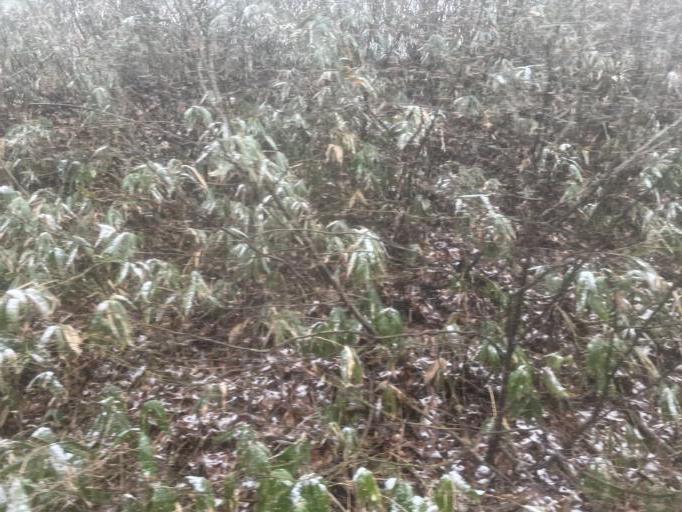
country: JP
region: Aomori
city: Goshogawara
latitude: 41.1014
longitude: 140.5281
